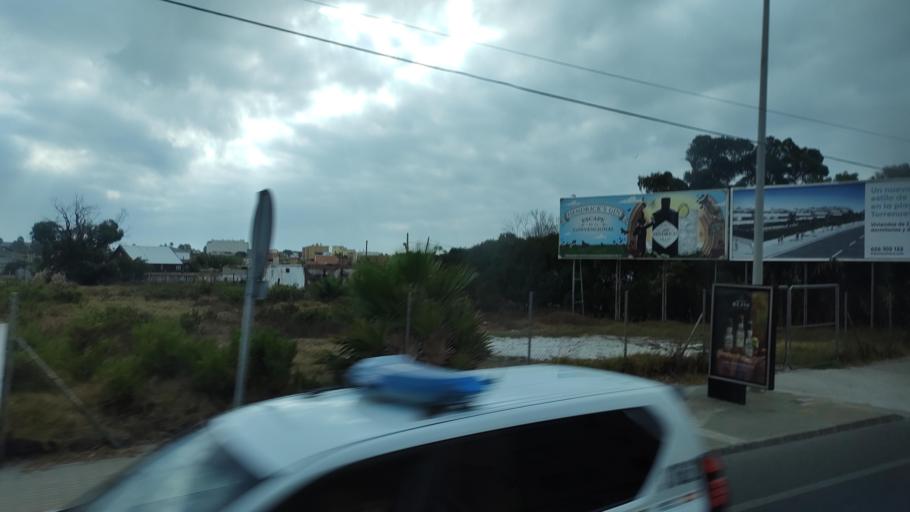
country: ES
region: Andalusia
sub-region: Provincia de Cadiz
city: La Linea de la Concepcion
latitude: 36.1712
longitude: -5.3712
